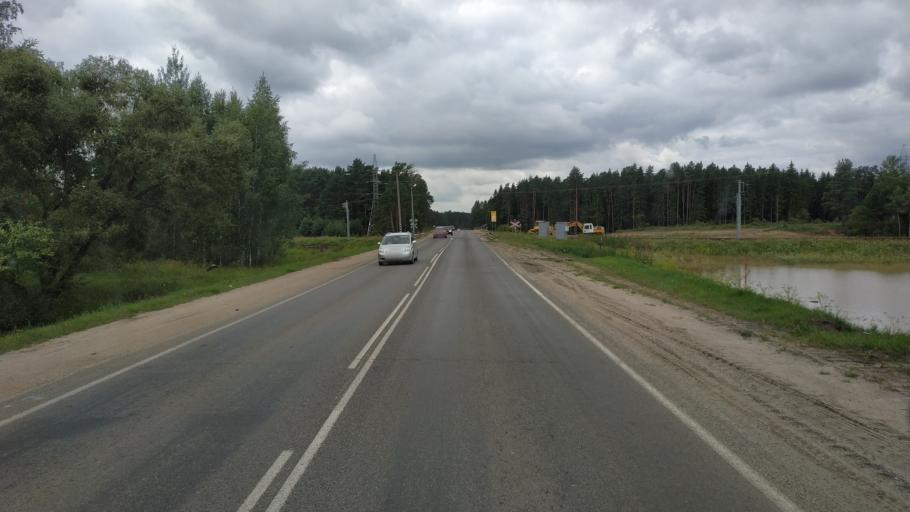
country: BY
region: Mogilev
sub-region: Mahilyowski Rayon
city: Veyno
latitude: 53.8757
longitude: 30.4286
